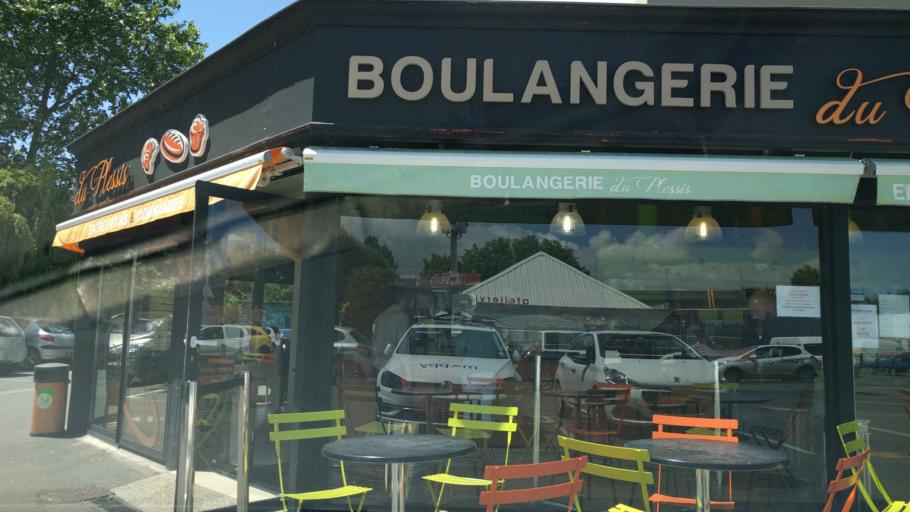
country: FR
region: Poitou-Charentes
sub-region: Departement de la Charente-Maritime
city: Puilboreau
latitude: 46.1621
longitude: -1.1240
